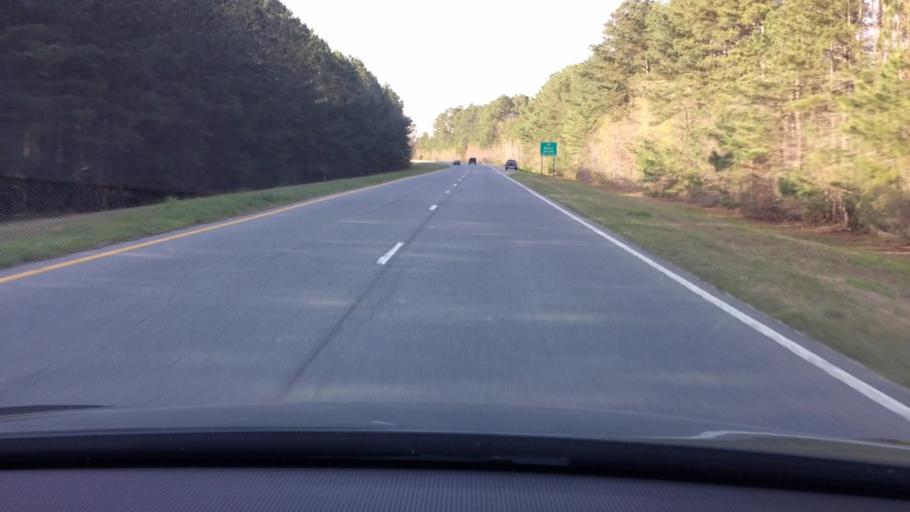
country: US
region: North Carolina
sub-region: Johnston County
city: Selma
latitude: 35.5110
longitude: -78.2818
